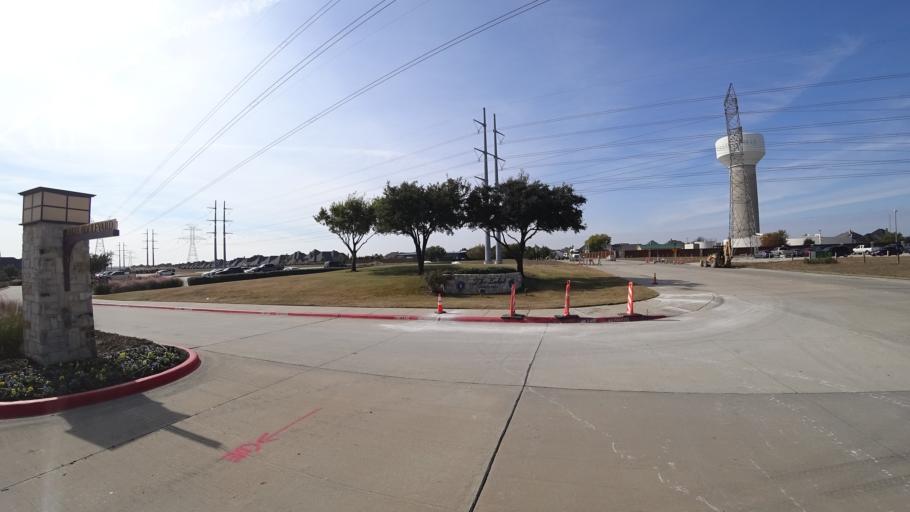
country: US
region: Texas
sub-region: Denton County
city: The Colony
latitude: 33.0426
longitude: -96.9063
